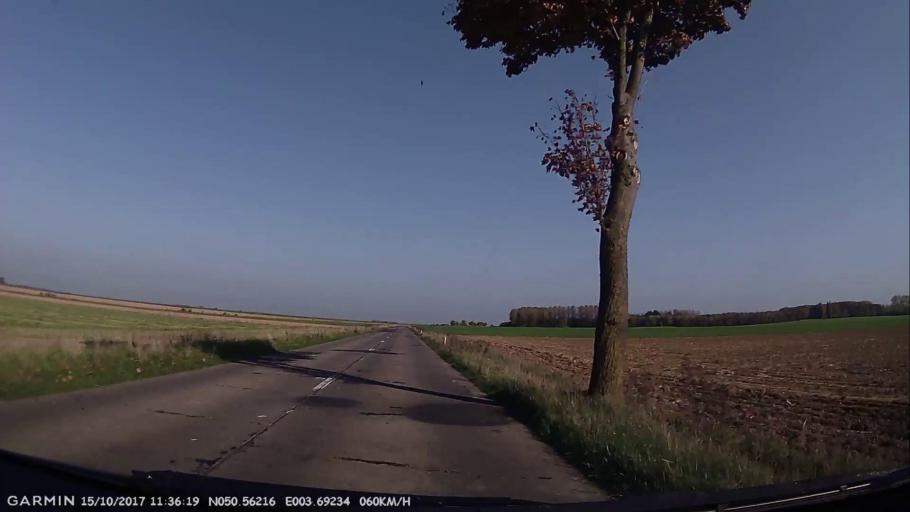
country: BE
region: Wallonia
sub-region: Province du Hainaut
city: Beloeil
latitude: 50.5624
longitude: 3.6918
